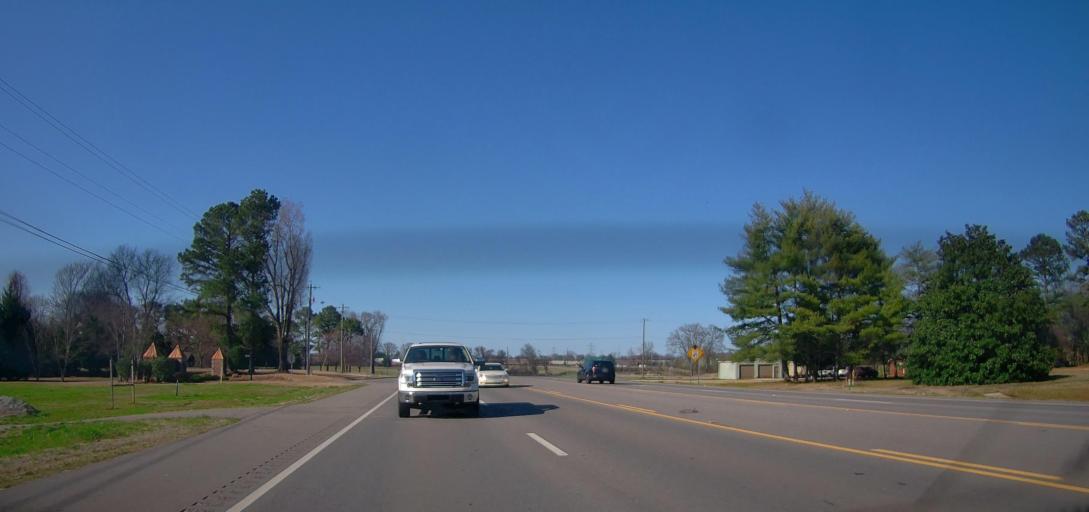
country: US
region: Alabama
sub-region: Colbert County
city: Muscle Shoals
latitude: 34.7086
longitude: -87.6348
